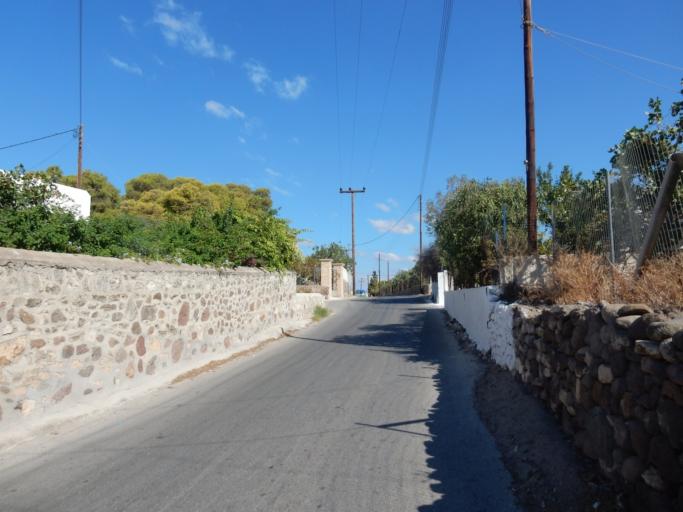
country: GR
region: Attica
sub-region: Nomos Piraios
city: Aegina
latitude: 37.7296
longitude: 23.4440
